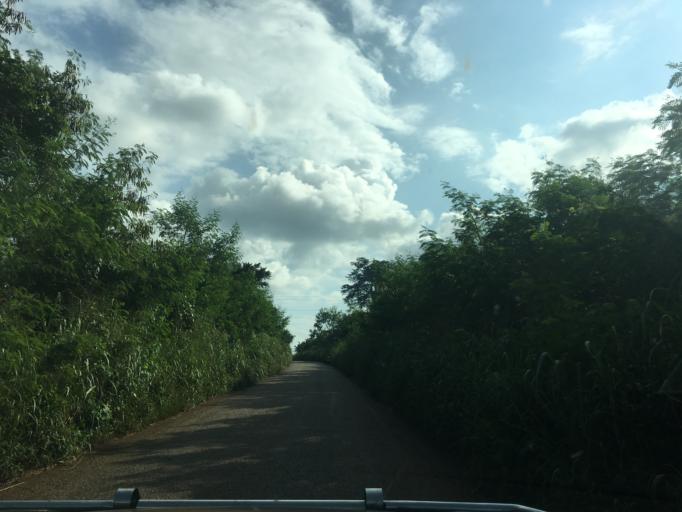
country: GH
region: Western
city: Bibiani
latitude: 6.7942
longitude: -2.5313
